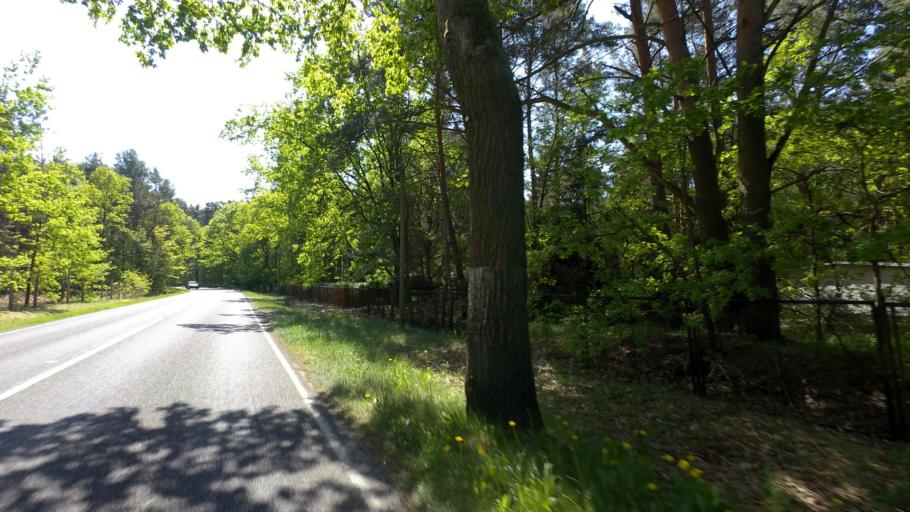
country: DE
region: Brandenburg
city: Bestensee
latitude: 52.2301
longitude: 13.6692
